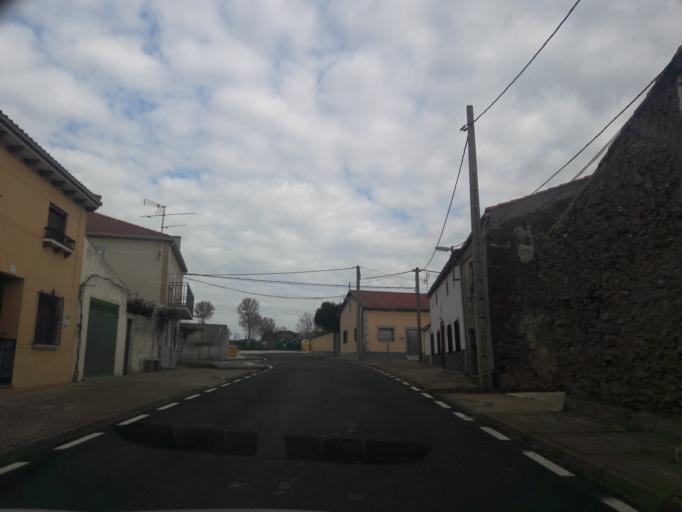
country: ES
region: Castille and Leon
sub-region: Provincia de Salamanca
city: Pastores
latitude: 40.4992
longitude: -6.5317
